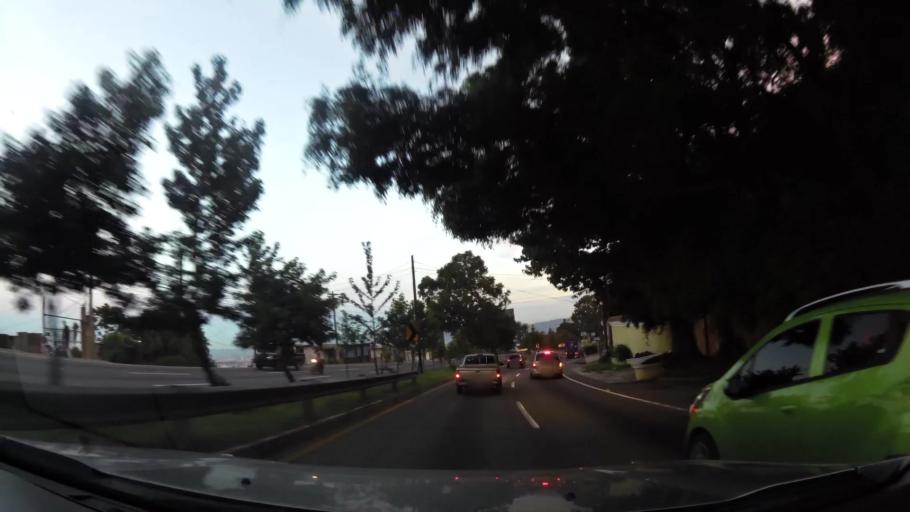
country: GT
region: Guatemala
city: Mixco
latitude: 14.6214
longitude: -90.6135
